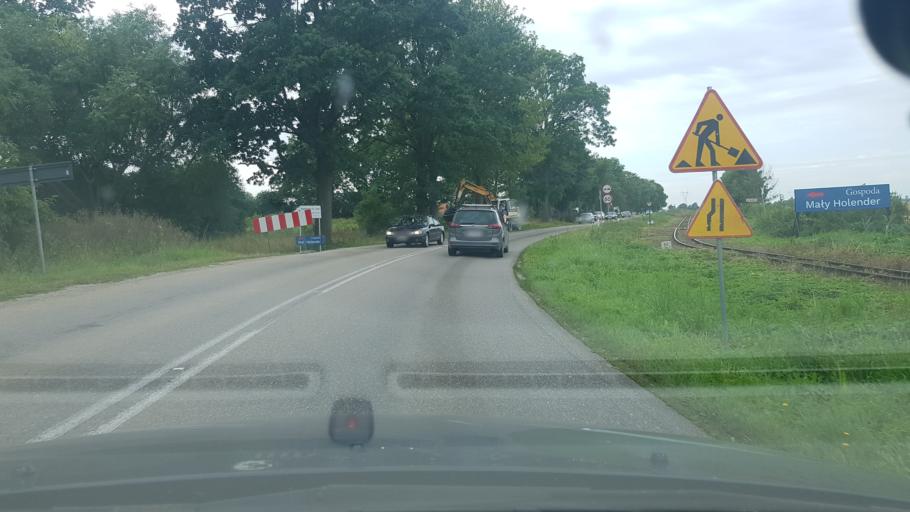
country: PL
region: Pomeranian Voivodeship
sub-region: Powiat nowodworski
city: Nowy Dwor Gdanski
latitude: 54.2426
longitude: 19.1421
